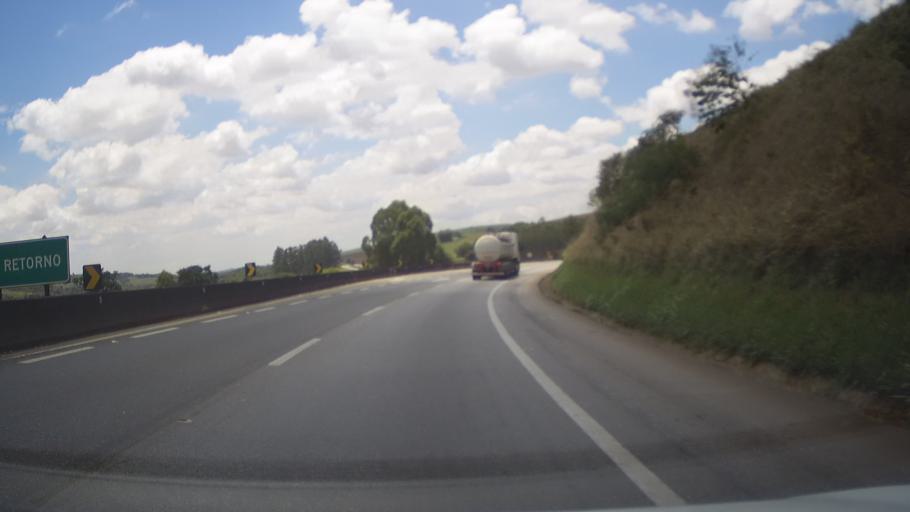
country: BR
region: Minas Gerais
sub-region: Campanha
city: Campanha
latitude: -21.8098
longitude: -45.4872
